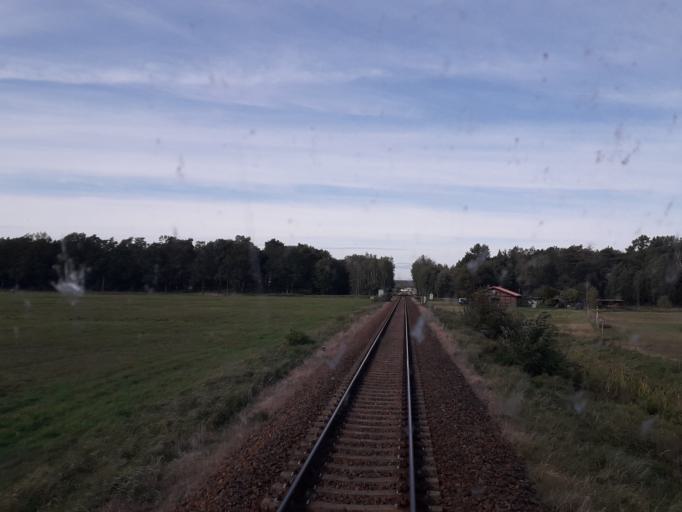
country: DE
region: Brandenburg
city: Kremmen
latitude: 52.7848
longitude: 13.0390
